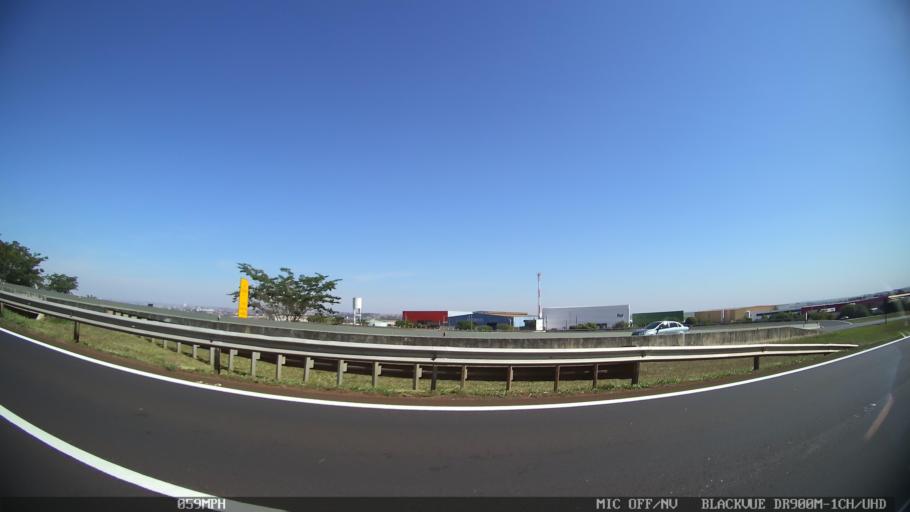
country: BR
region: Sao Paulo
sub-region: Jardinopolis
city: Jardinopolis
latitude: -21.0922
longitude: -47.7969
